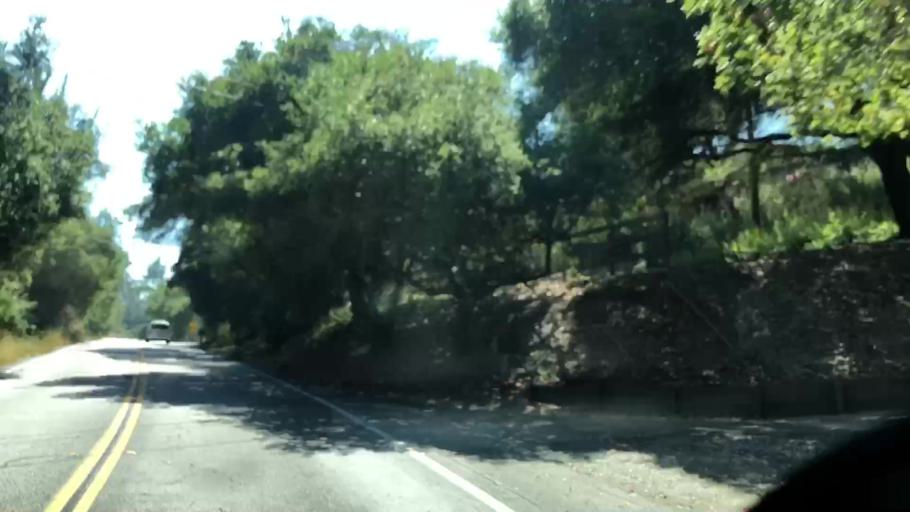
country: US
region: California
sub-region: Santa Cruz County
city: Corralitos
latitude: 36.9941
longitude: -121.8172
